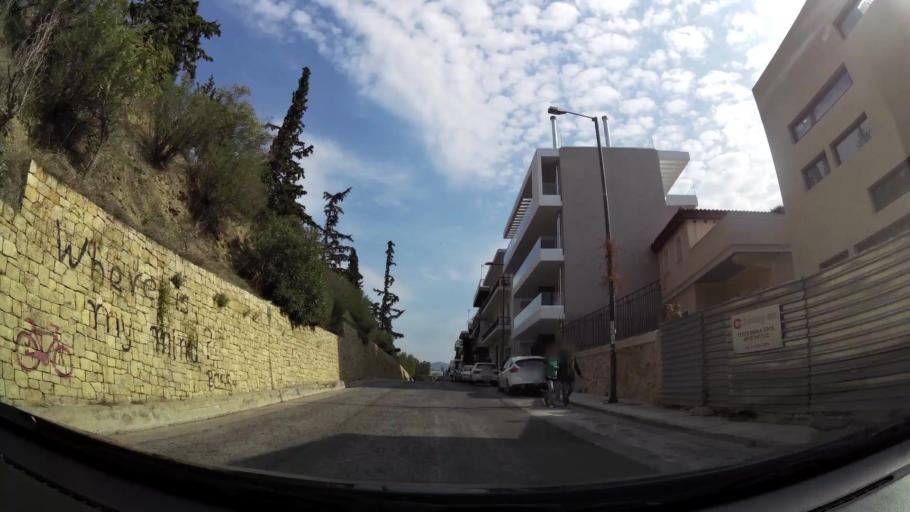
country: GR
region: Attica
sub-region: Nomarchia Athinas
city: Athens
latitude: 37.9651
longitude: 23.7184
